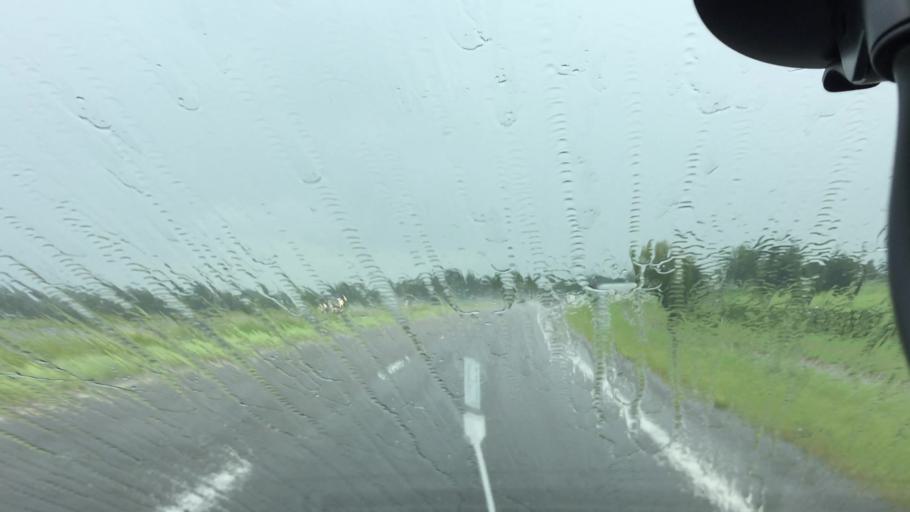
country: US
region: Alabama
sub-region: Montgomery County
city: Pike Road
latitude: 32.2280
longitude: -86.1193
